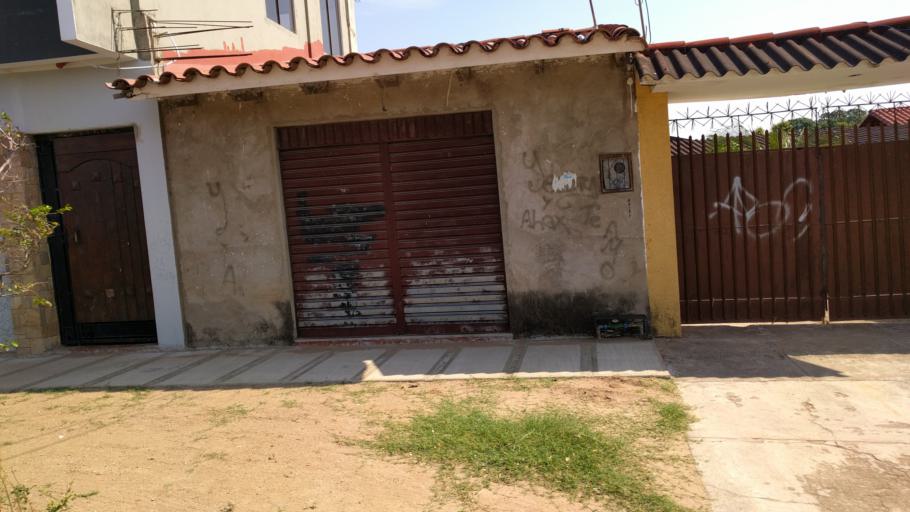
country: BO
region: Santa Cruz
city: Santa Cruz de la Sierra
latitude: -17.8169
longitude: -63.1698
